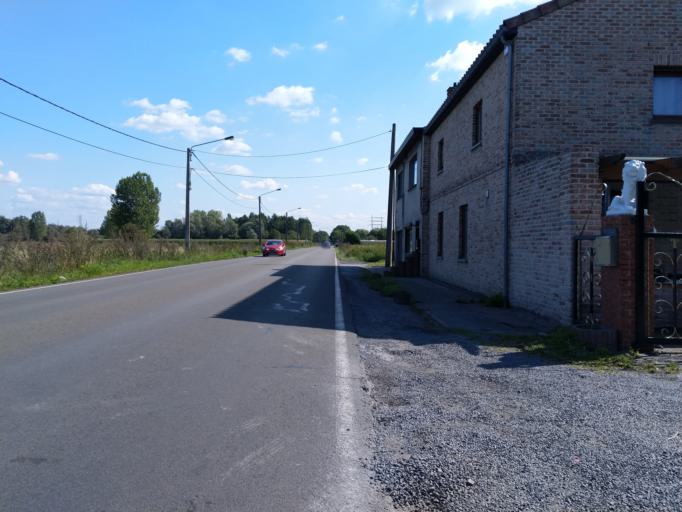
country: BE
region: Wallonia
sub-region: Province du Hainaut
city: Quaregnon
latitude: 50.4591
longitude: 3.8449
